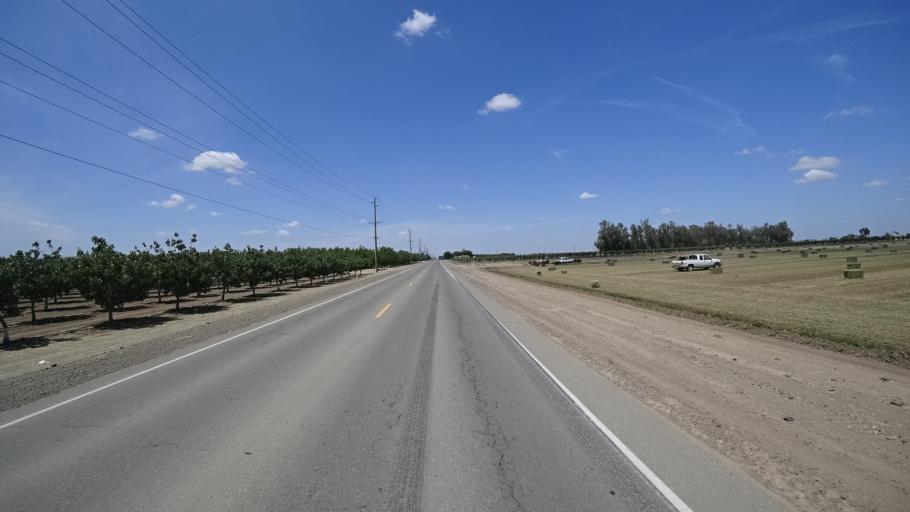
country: US
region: California
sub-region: Kings County
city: Home Garden
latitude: 36.2986
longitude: -119.5596
